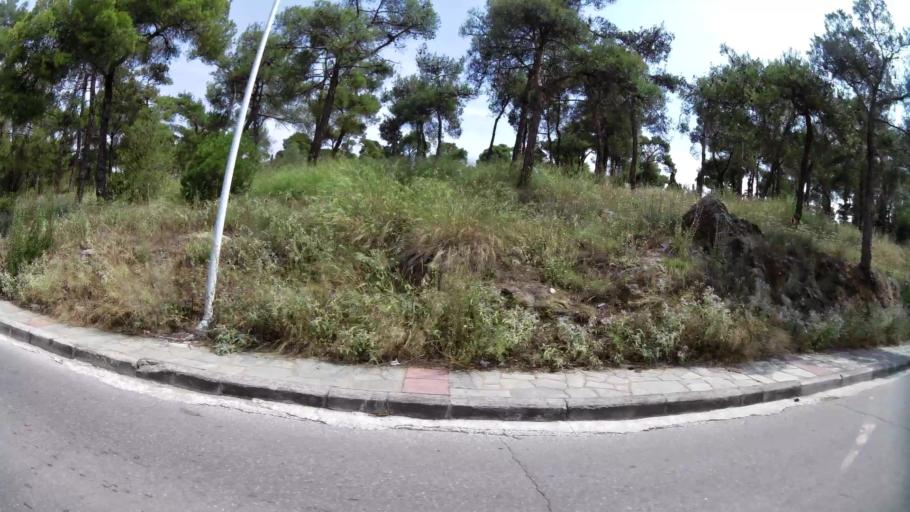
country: GR
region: Central Macedonia
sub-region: Nomos Thessalonikis
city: Agios Pavlos
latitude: 40.6350
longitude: 22.9664
